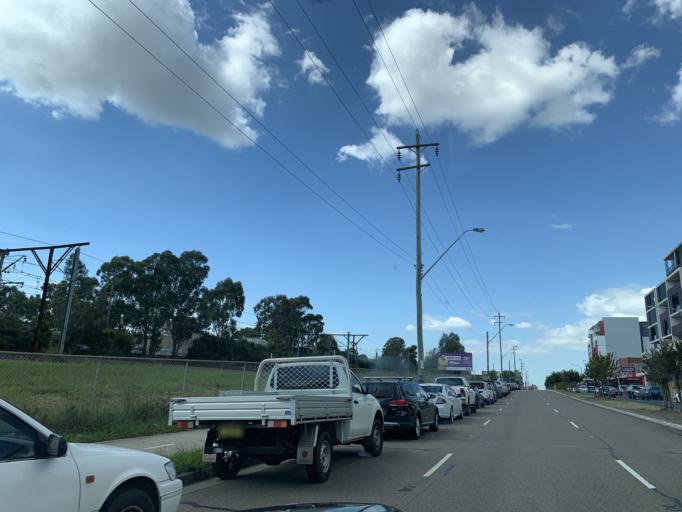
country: AU
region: New South Wales
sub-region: Penrith Municipality
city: Kingswood Park
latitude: -33.7578
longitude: 150.7166
